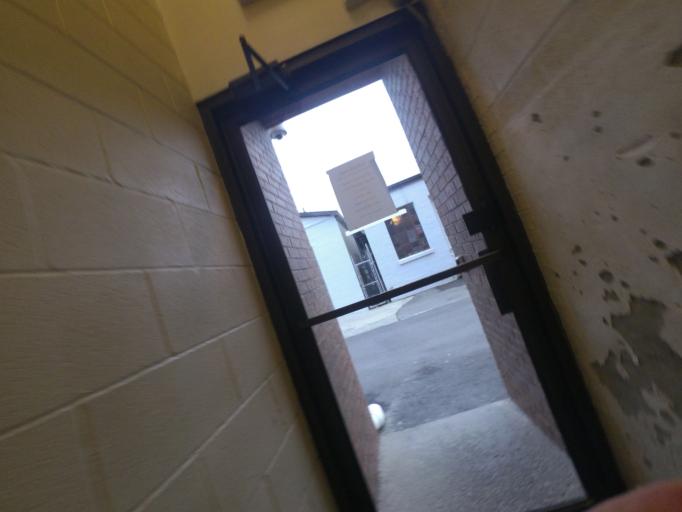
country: CN
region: Xinjiang Uygur Zizhiqu
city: Ayxin Siri
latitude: 43.4640
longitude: 80.5211
